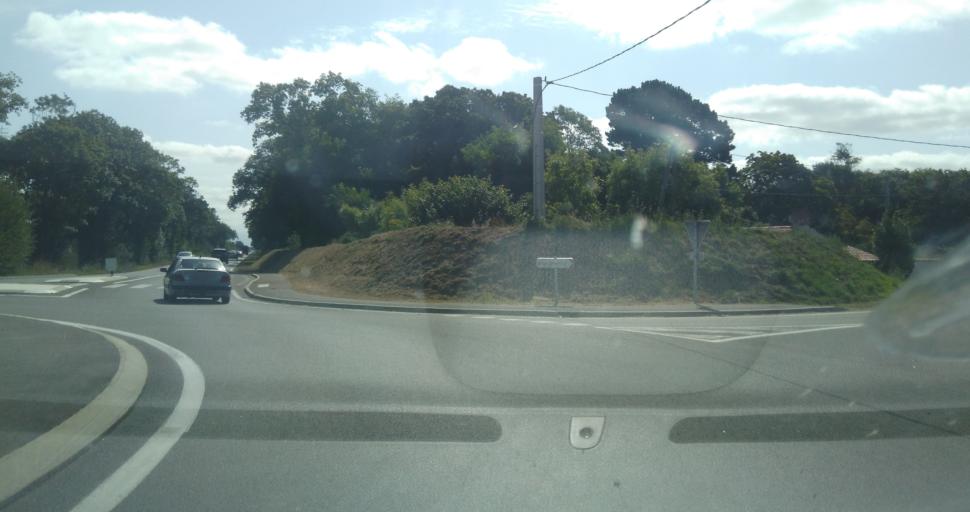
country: FR
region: Pays de la Loire
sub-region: Departement de la Vendee
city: Chateau-d'Olonne
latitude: 46.4780
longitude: -1.6797
